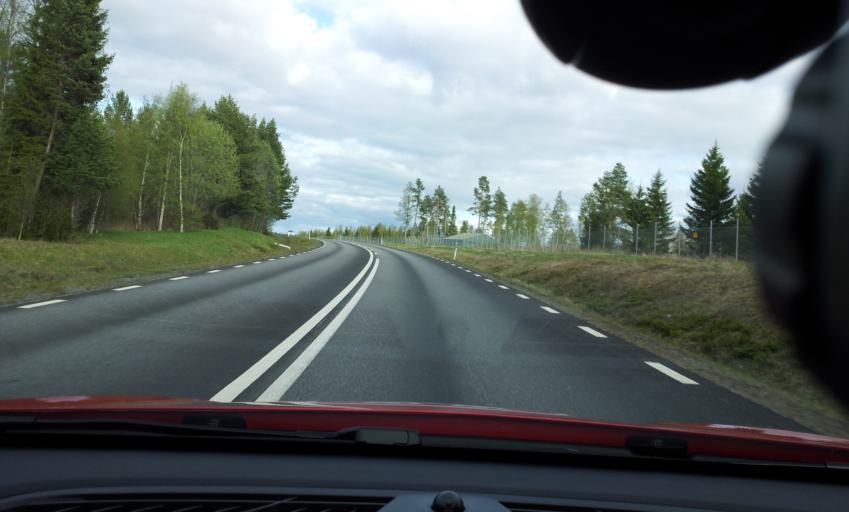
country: SE
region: Jaemtland
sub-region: Krokoms Kommun
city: Krokom
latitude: 63.2043
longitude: 14.4777
